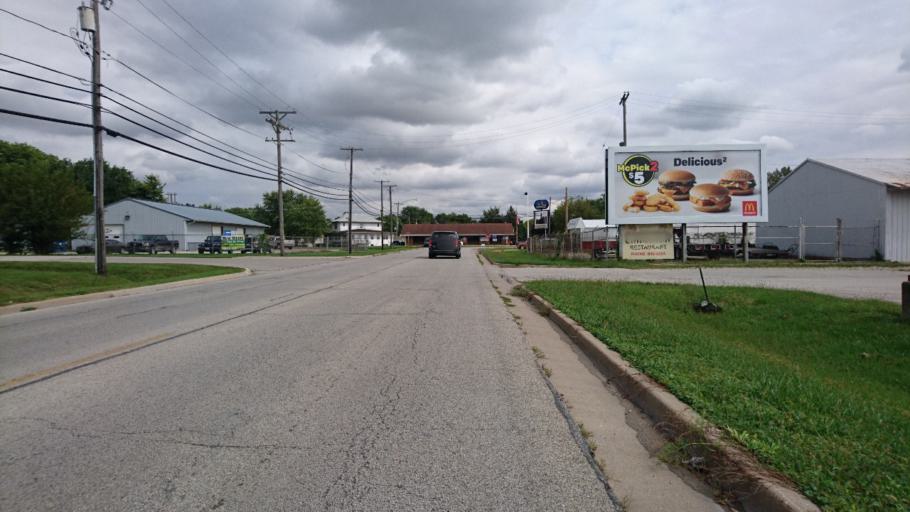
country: US
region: Illinois
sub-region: Livingston County
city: Pontiac
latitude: 40.8864
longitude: -88.6401
